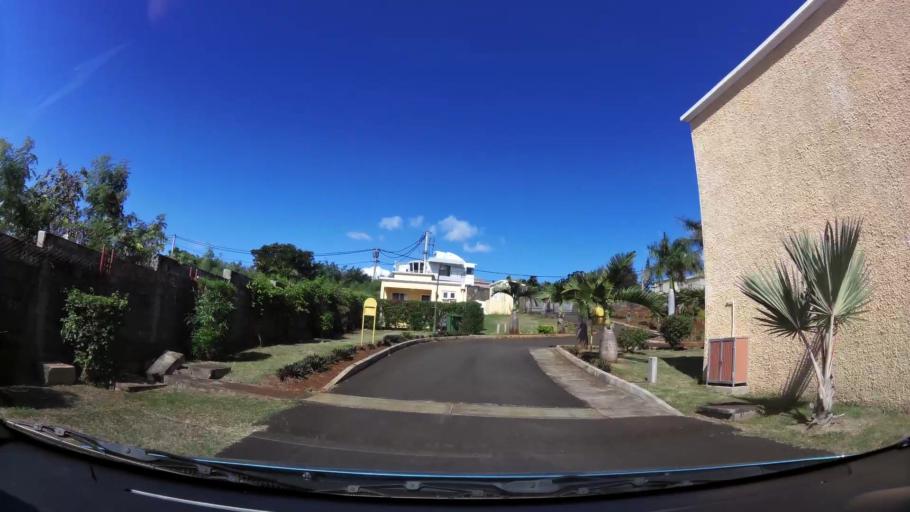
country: MU
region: Black River
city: Albion
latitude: -20.2211
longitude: 57.4155
